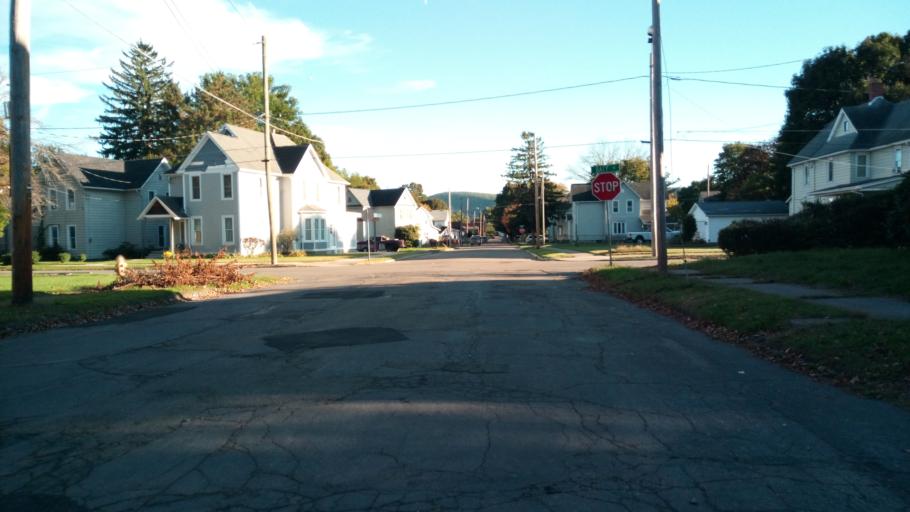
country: US
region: New York
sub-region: Chemung County
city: Elmira
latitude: 42.0737
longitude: -76.8072
